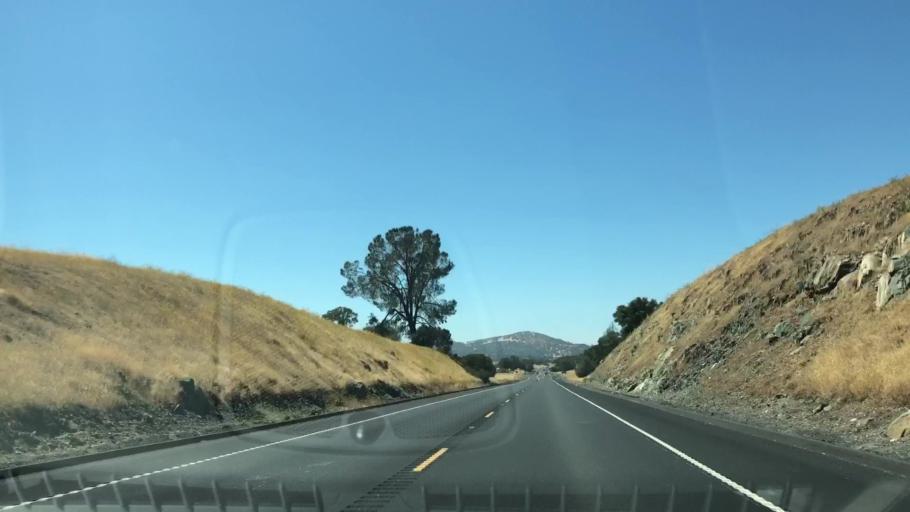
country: US
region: California
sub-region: Calaveras County
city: Copperopolis
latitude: 37.9782
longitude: -120.6482
